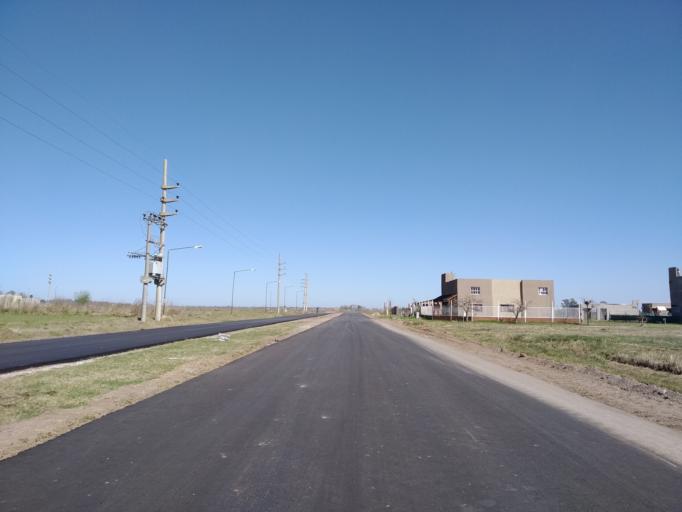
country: AR
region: Santa Fe
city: Funes
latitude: -32.8989
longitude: -60.8146
